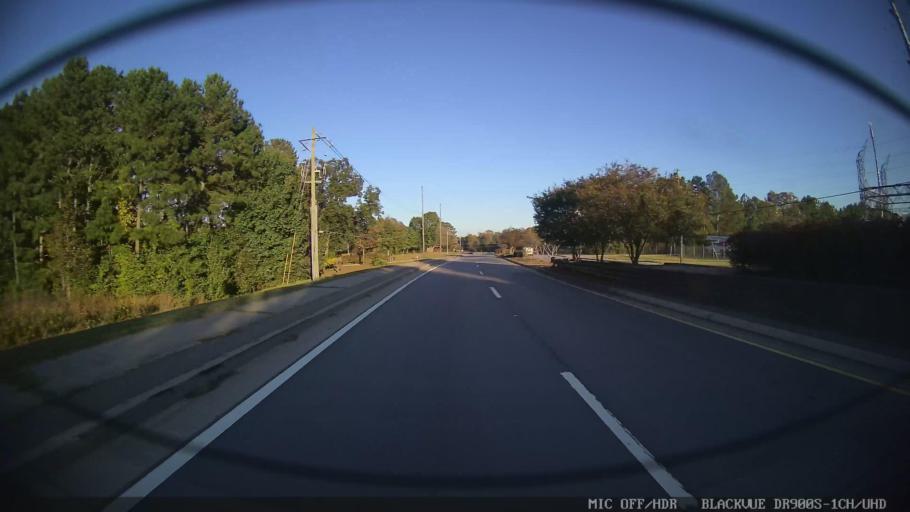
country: US
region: Georgia
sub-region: Clayton County
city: Jonesboro
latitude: 33.5359
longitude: -84.3119
